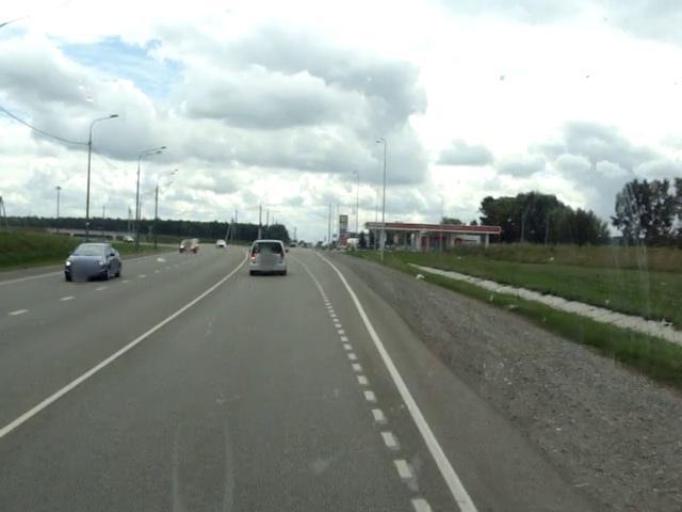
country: RU
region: Altai Krai
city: Zarya
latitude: 52.5810
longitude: 85.1753
